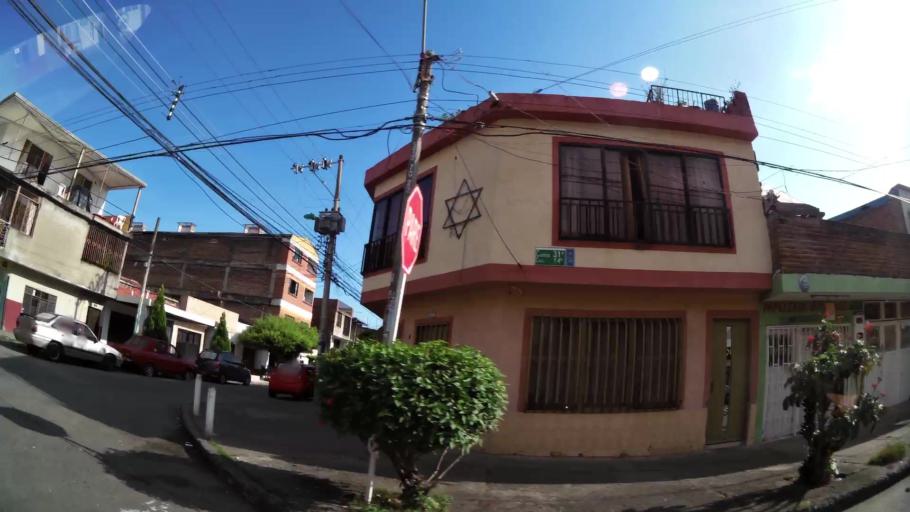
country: CO
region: Valle del Cauca
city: Cali
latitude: 3.4265
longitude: -76.5270
